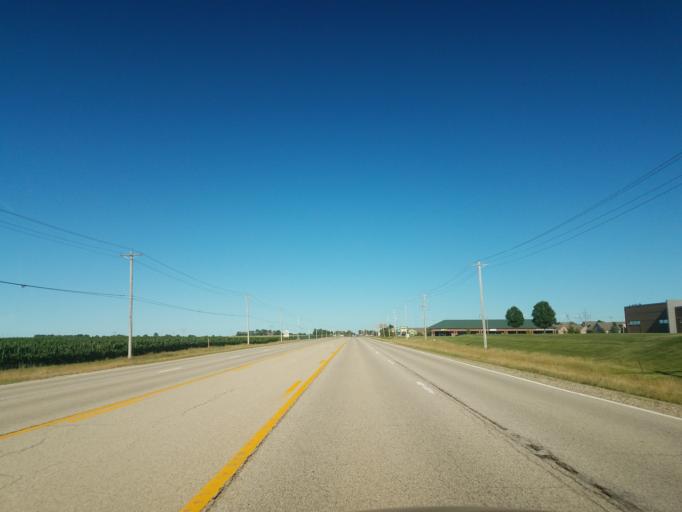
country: US
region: Illinois
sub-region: McLean County
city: Downs
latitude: 40.4583
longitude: -88.9125
